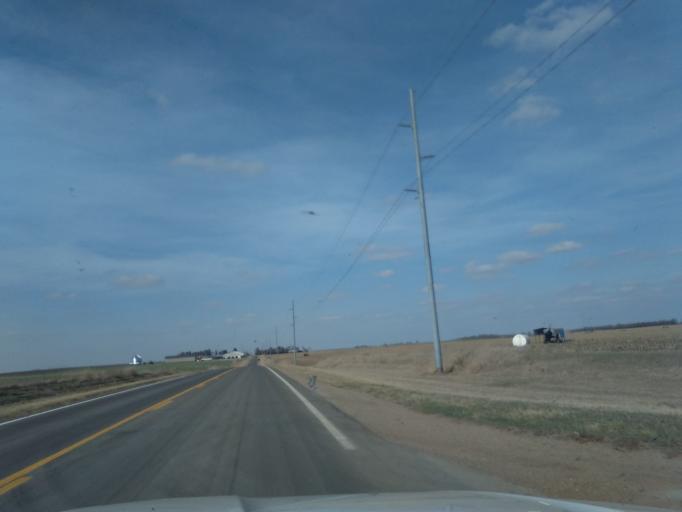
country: US
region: Nebraska
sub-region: Gage County
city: Beatrice
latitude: 40.1902
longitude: -96.9353
